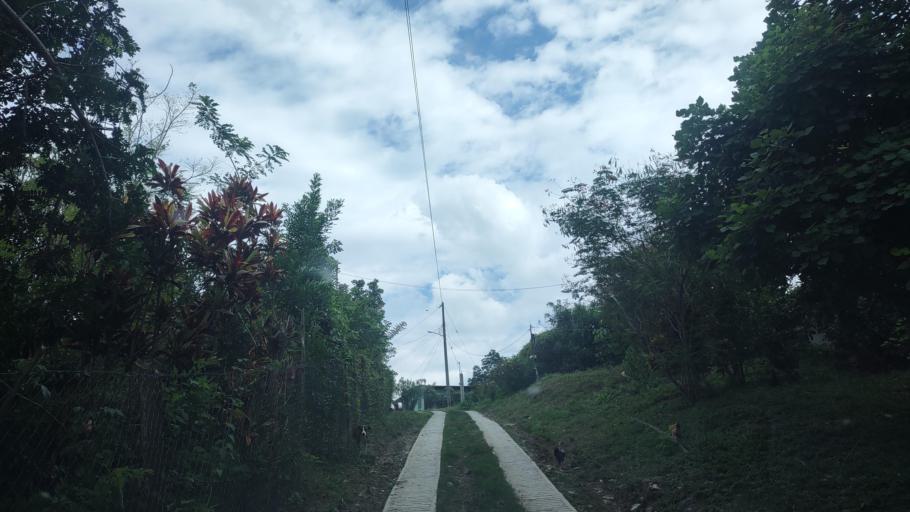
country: MX
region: Veracruz
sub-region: Ixcatepec
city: Ixcatepec
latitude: 21.2145
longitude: -97.9830
